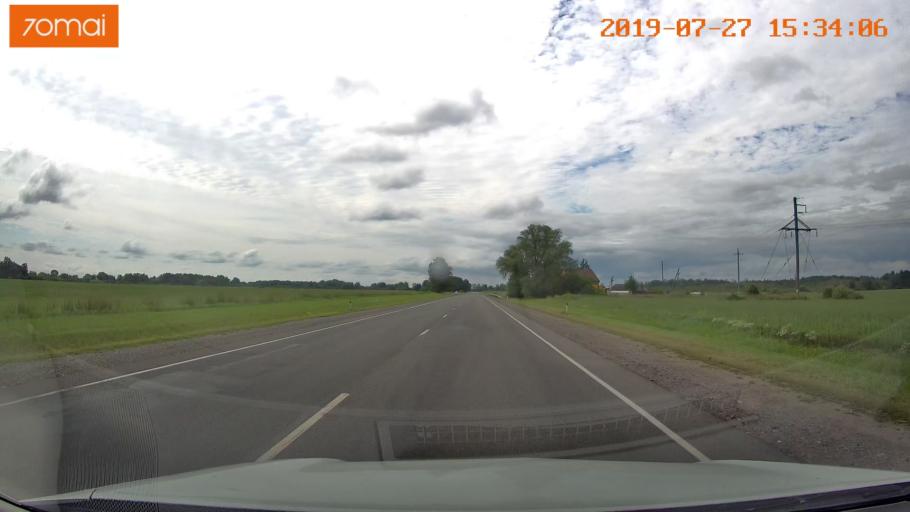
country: RU
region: Kaliningrad
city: Nesterov
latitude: 54.6120
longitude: 22.4334
